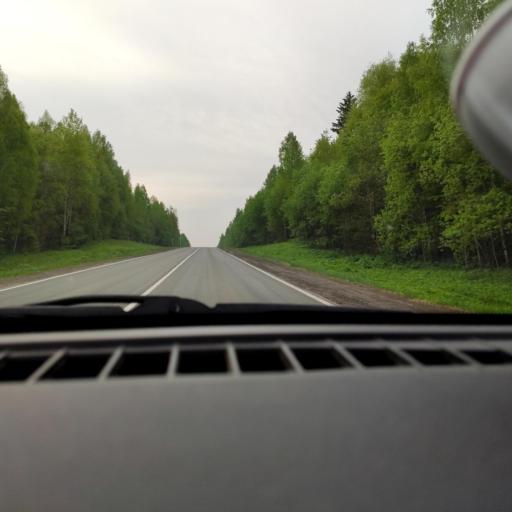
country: RU
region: Perm
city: Perm
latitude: 58.1547
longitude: 56.2524
